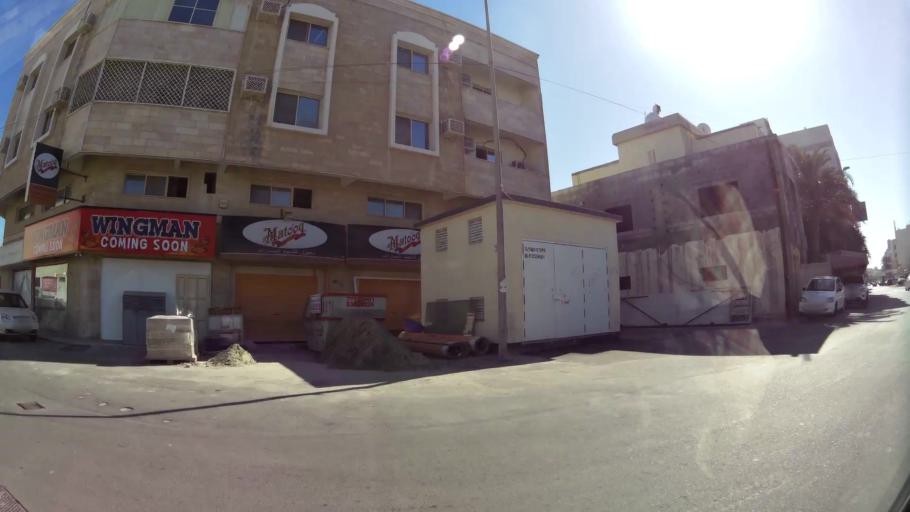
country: BH
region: Muharraq
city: Al Muharraq
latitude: 26.2632
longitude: 50.6163
